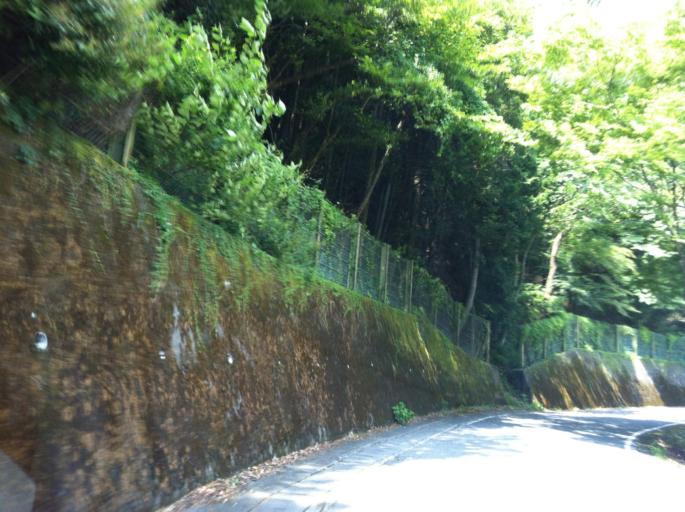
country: JP
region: Shizuoka
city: Shizuoka-shi
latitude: 35.2419
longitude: 138.3409
